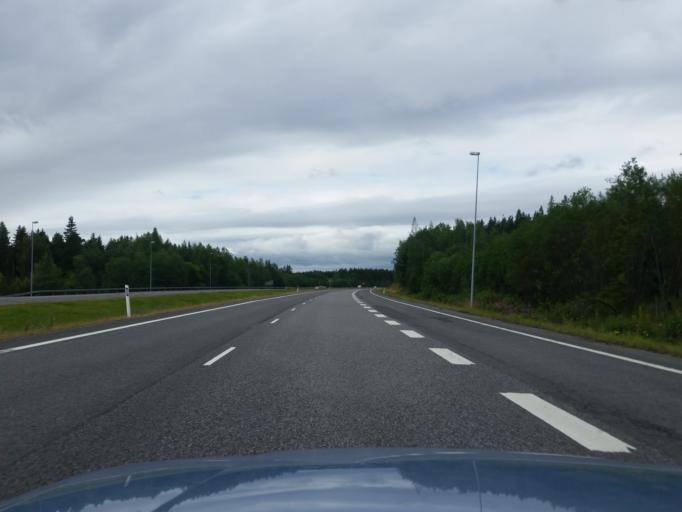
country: FI
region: Varsinais-Suomi
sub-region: Turku
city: Kaarina
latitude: 60.4276
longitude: 22.4383
